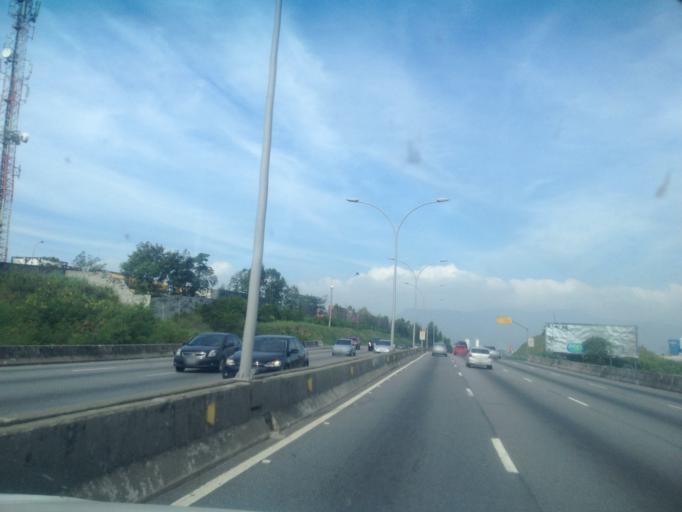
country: BR
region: Rio de Janeiro
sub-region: Rio De Janeiro
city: Rio de Janeiro
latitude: -22.8711
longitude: -43.2323
